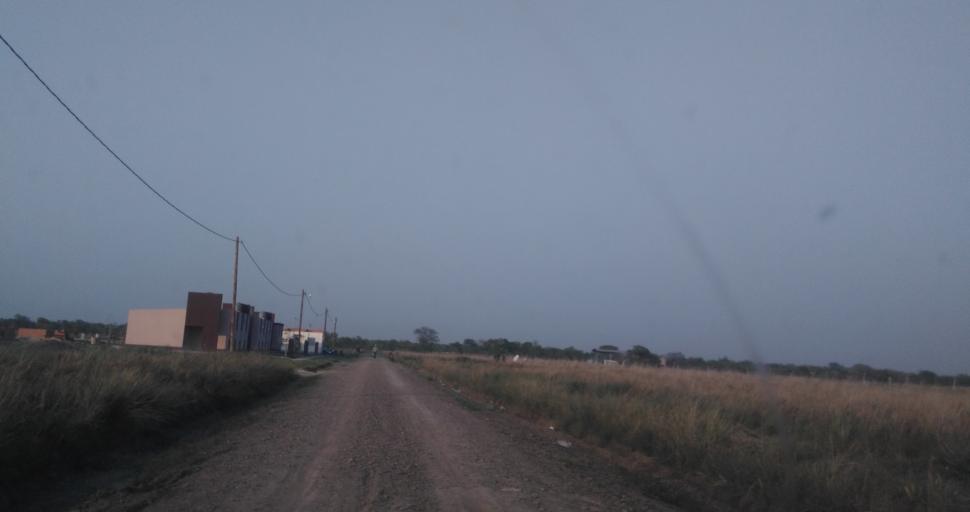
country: AR
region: Chaco
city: Resistencia
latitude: -27.4850
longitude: -59.0146
